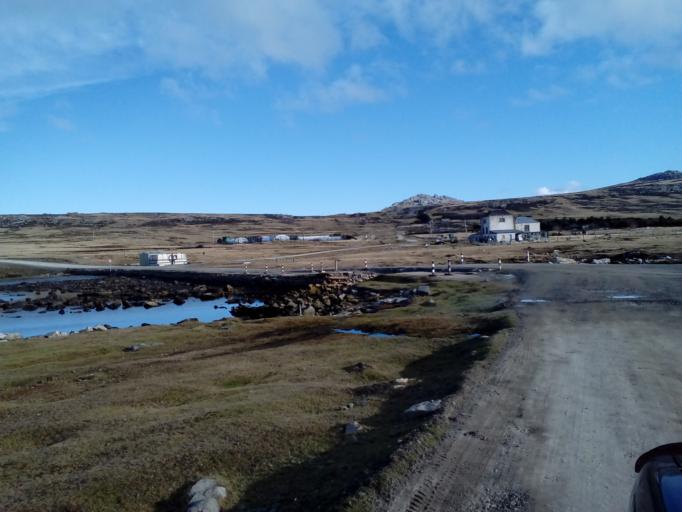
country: FK
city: Stanley
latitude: -51.6854
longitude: -57.9205
